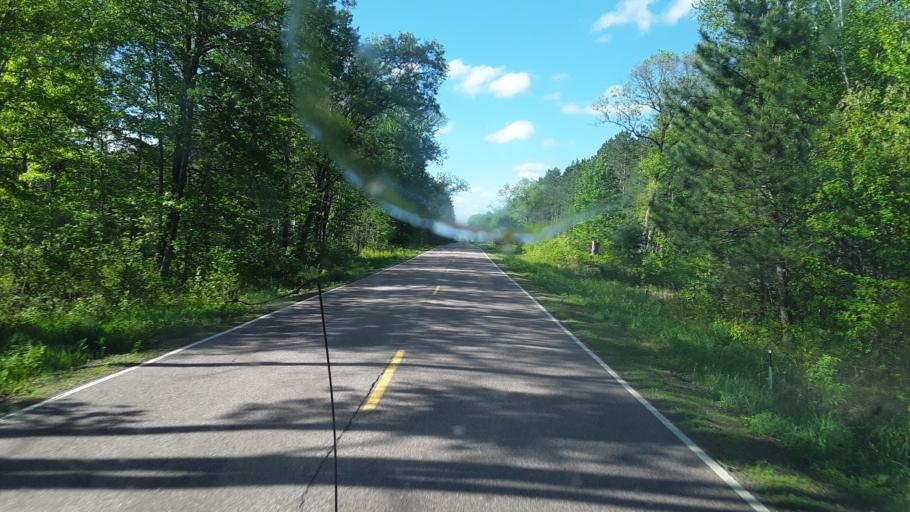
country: US
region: Wisconsin
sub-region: Wood County
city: Nekoosa
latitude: 44.3672
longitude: -90.1301
